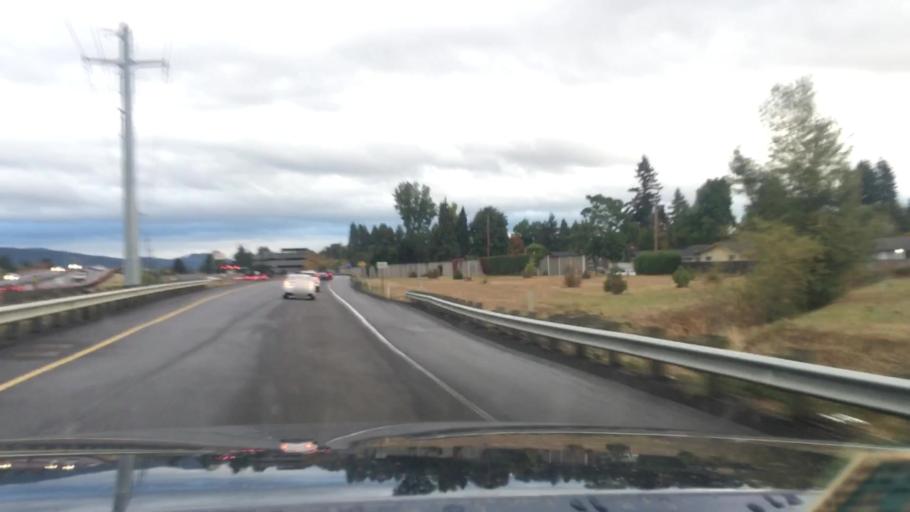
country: US
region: Oregon
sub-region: Lane County
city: Eugene
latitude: 44.0876
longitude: -123.0735
